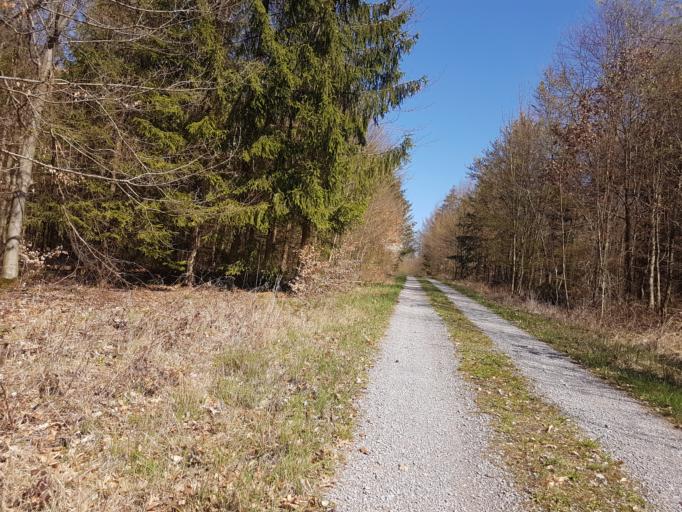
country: DE
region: Baden-Wuerttemberg
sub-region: Regierungsbezirk Stuttgart
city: Jagsthausen
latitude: 49.3390
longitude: 9.4873
